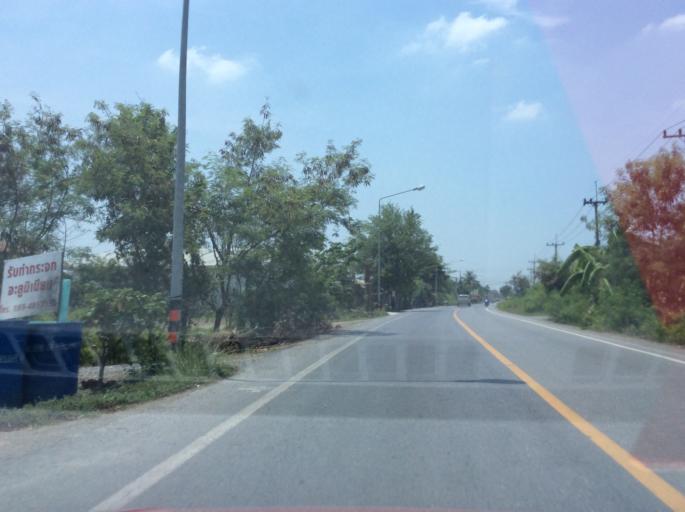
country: TH
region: Pathum Thani
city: Ban Lam Luk Ka
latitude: 13.9931
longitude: 100.7778
